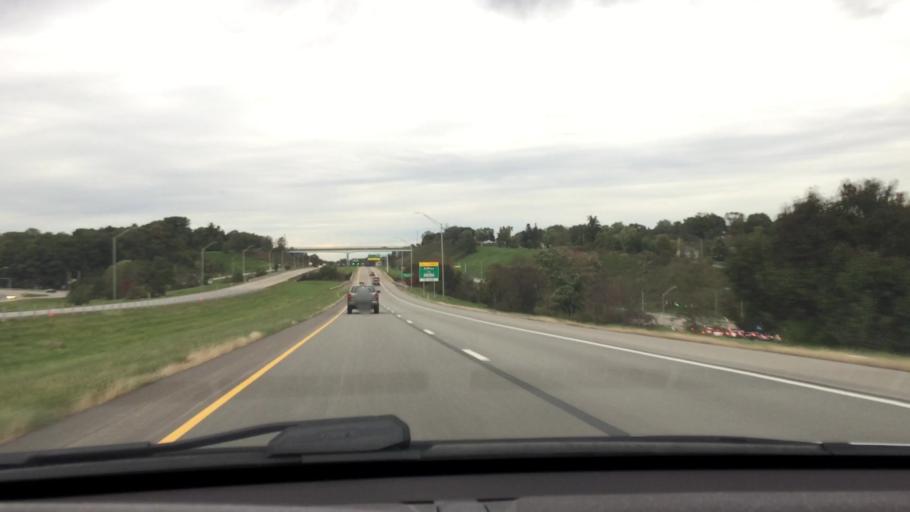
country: US
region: Pennsylvania
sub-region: Beaver County
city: West Mayfield
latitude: 40.7609
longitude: -80.3637
